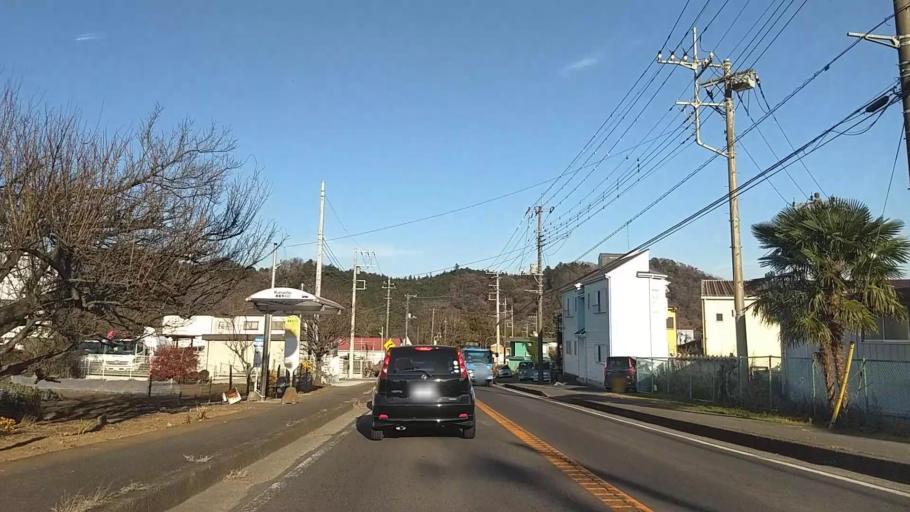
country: JP
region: Kanagawa
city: Zama
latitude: 35.5328
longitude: 139.2793
